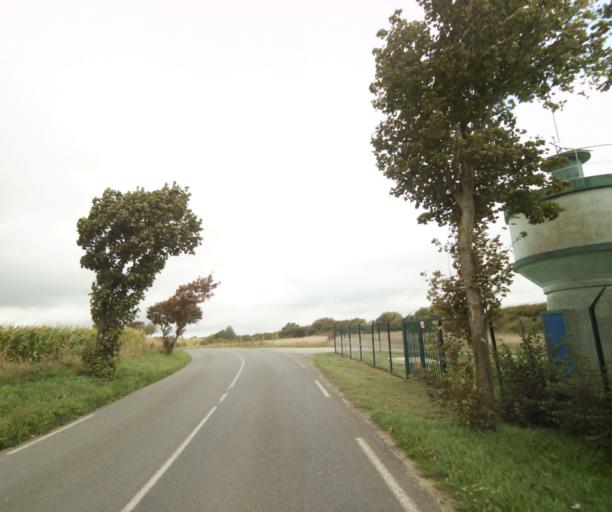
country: FR
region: Nord-Pas-de-Calais
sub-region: Departement du Pas-de-Calais
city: Etaples
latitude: 50.5303
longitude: 1.6818
